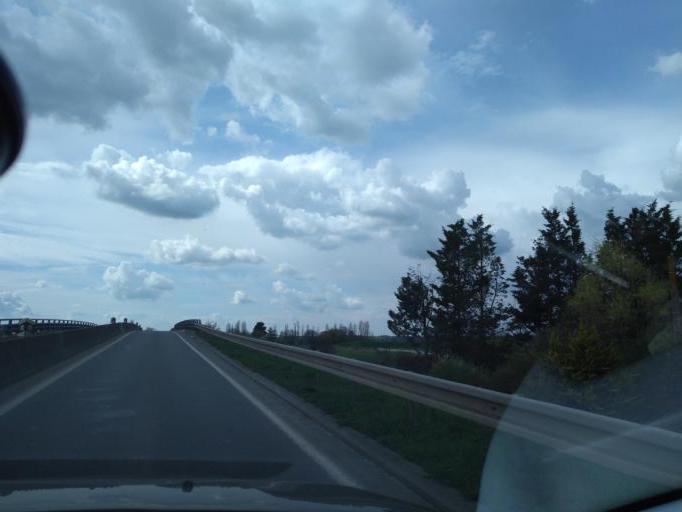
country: FR
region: Pays de la Loire
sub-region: Departement de Maine-et-Loire
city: Avrille
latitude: 47.5146
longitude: -0.6184
